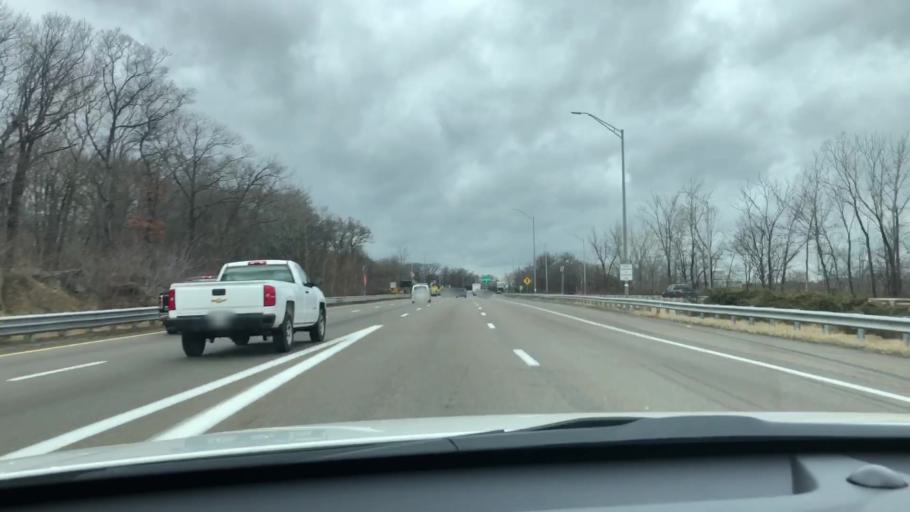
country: US
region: Massachusetts
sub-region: Norfolk County
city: Braintree
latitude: 42.2299
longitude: -71.0207
